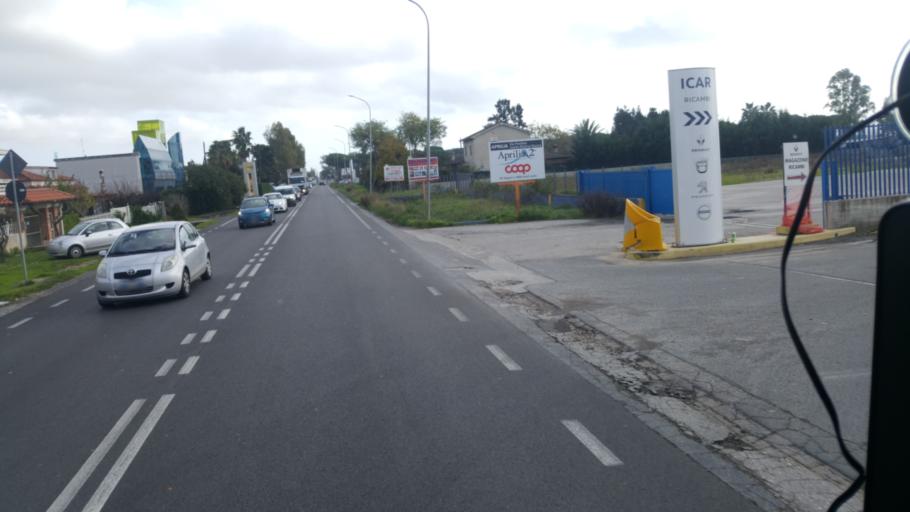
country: IT
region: Latium
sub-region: Provincia di Latina
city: Borgo Podgora
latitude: 41.4808
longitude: 12.8668
